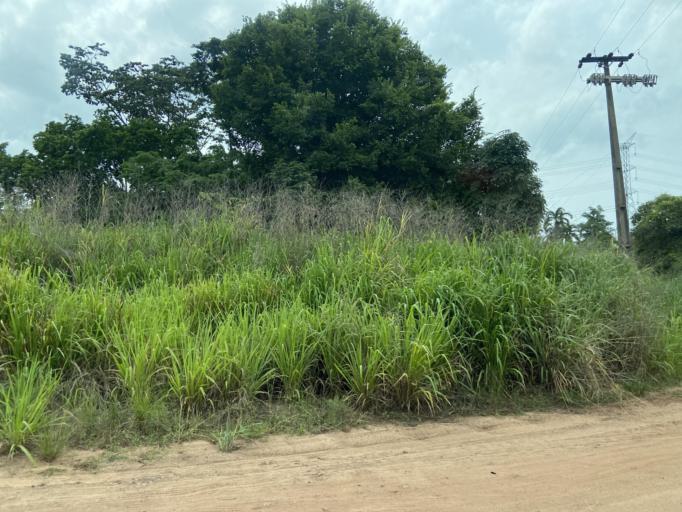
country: BR
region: Para
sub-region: Maraba
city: Maraba
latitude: -5.2890
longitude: -49.0551
